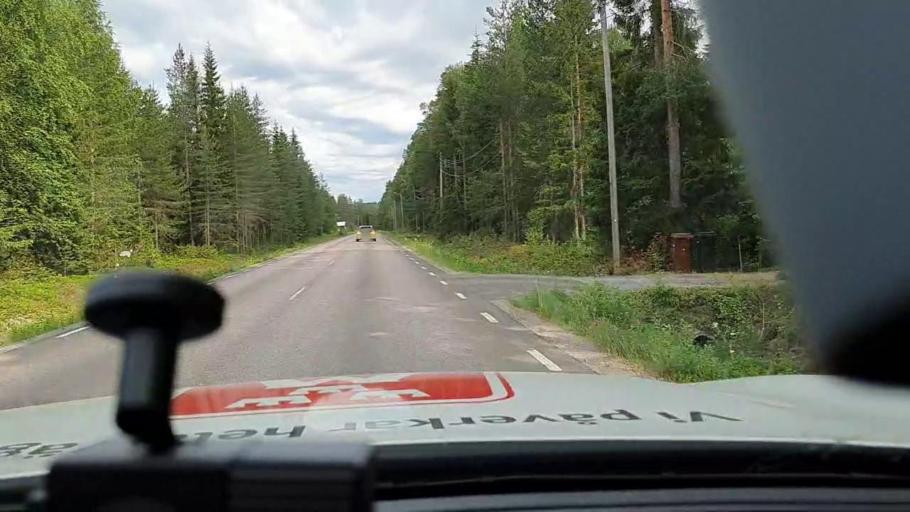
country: SE
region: Norrbotten
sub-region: Bodens Kommun
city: Saevast
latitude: 65.7270
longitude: 21.7456
